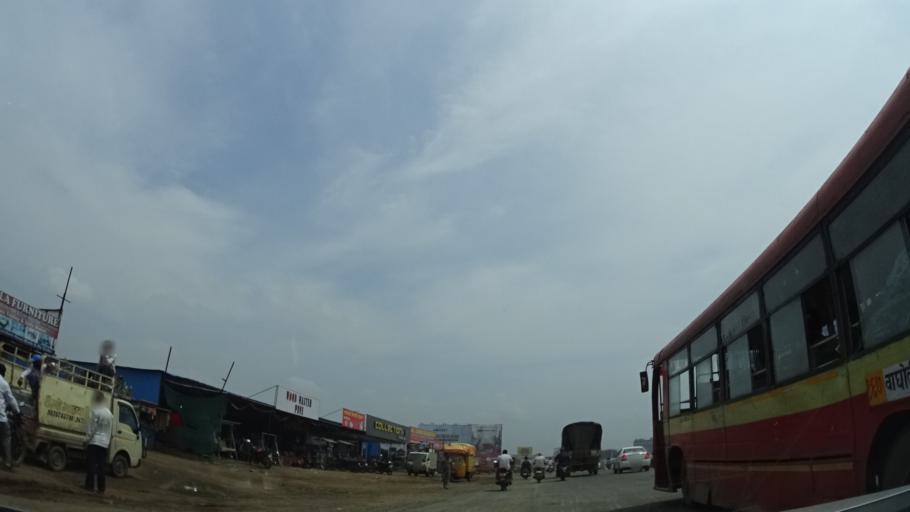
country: IN
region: Maharashtra
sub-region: Pune Division
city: Lohogaon
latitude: 18.5692
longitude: 73.9507
